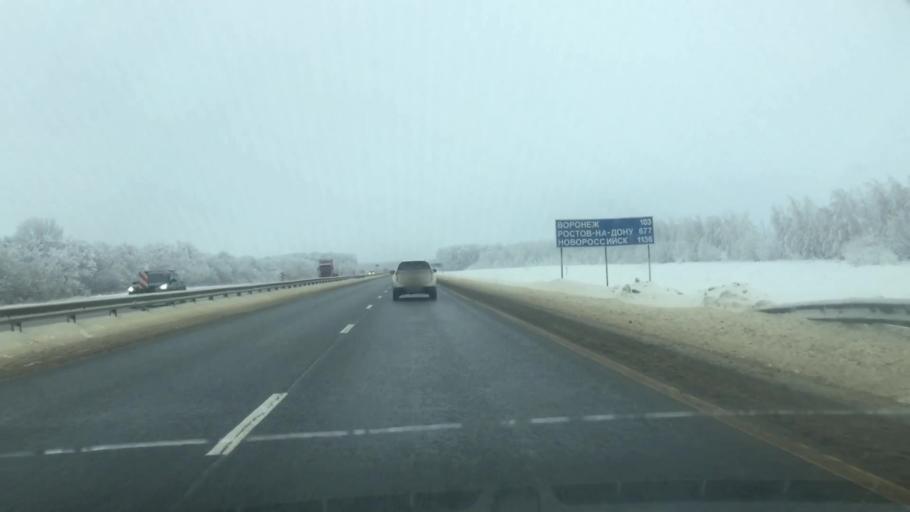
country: RU
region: Lipetsk
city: Zadonsk
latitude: 52.4988
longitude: 38.7553
